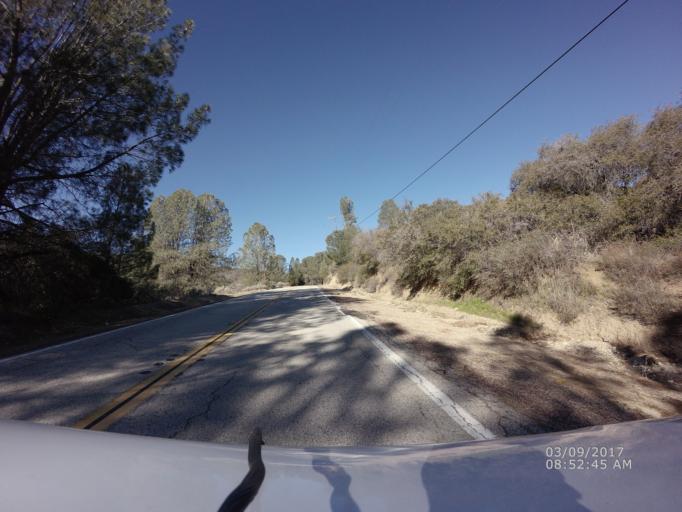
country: US
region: California
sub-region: Los Angeles County
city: Green Valley
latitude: 34.7107
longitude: -118.5526
